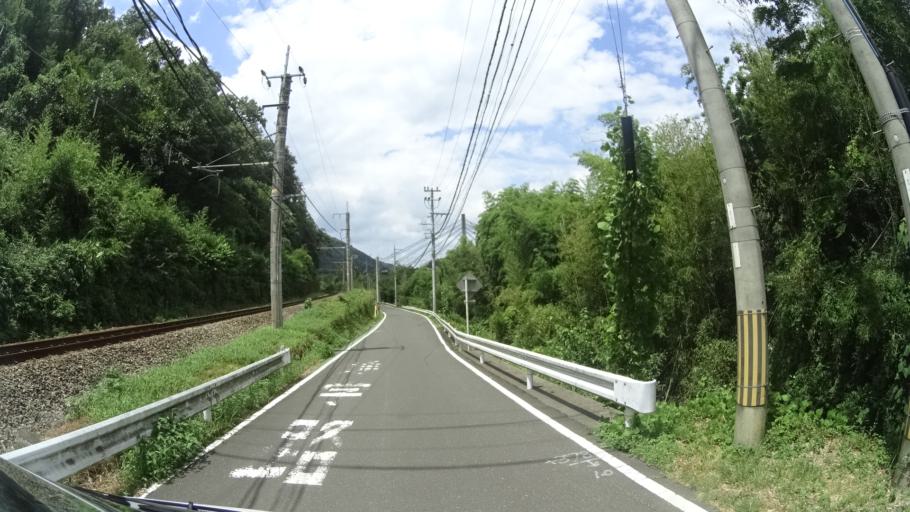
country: JP
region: Kyoto
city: Ayabe
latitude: 35.2896
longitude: 135.2696
